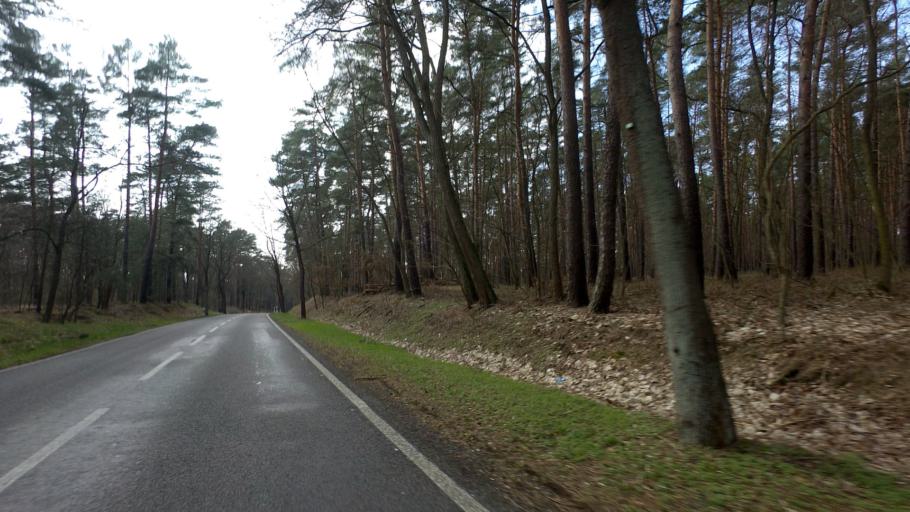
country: DE
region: Brandenburg
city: Dahme
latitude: 51.9502
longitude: 13.4038
